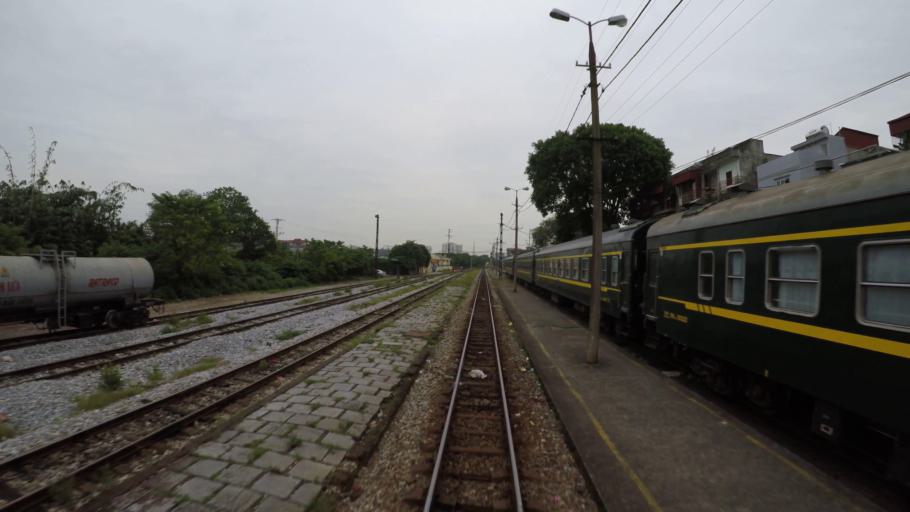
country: VN
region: Ha Noi
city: Trau Quy
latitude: 21.0316
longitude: 105.9101
